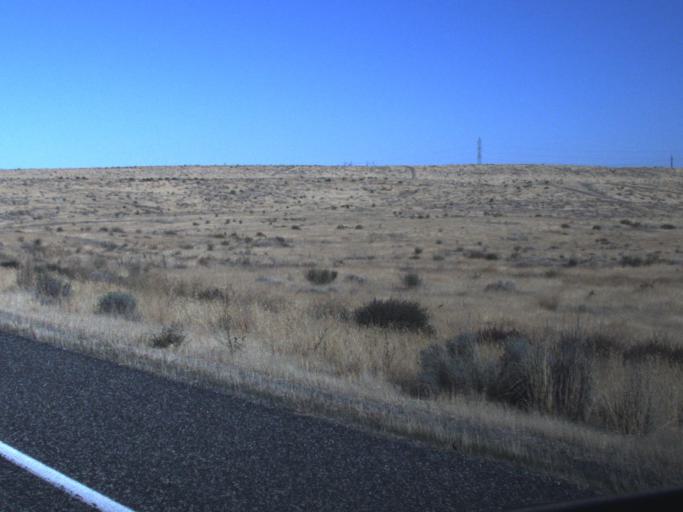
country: US
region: Washington
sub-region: Benton County
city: West Richland
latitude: 46.3563
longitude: -119.3732
